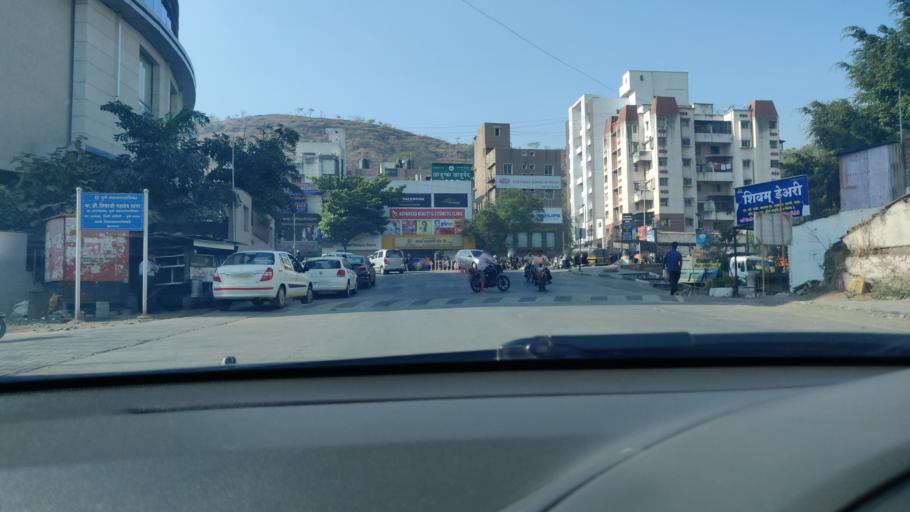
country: IN
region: Maharashtra
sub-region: Pune Division
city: Khadki
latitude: 18.5592
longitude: 73.7922
